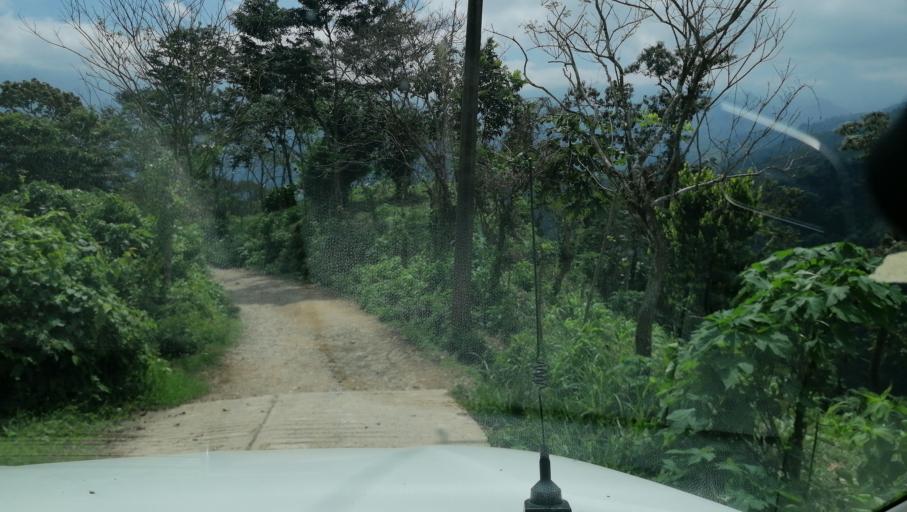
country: MX
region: Chiapas
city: Ixtacomitan
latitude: 17.3574
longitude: -93.1203
